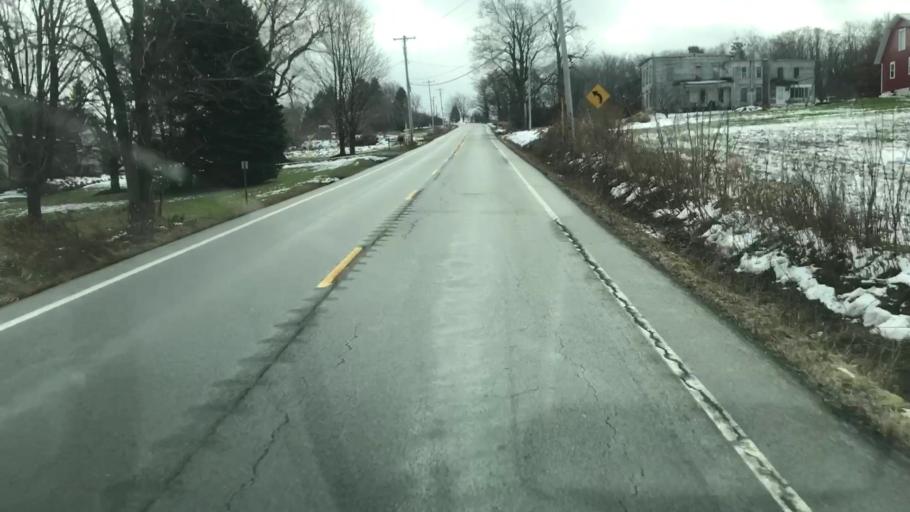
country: US
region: New York
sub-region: Onondaga County
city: Skaneateles
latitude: 42.8508
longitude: -76.3932
